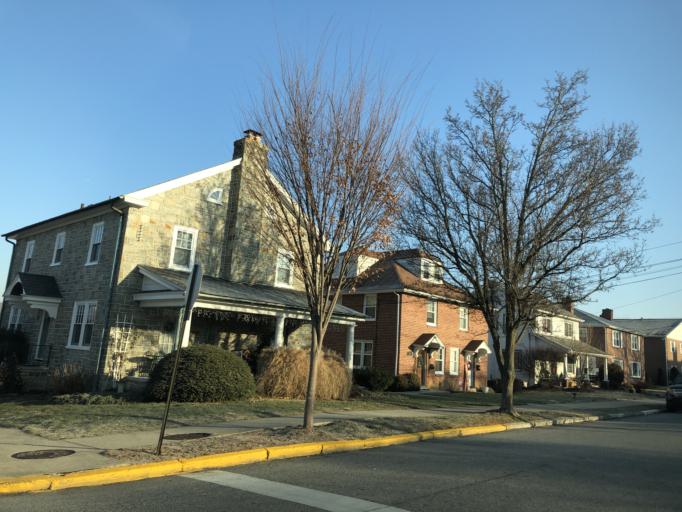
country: US
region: Pennsylvania
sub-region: Chester County
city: Downingtown
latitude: 40.0029
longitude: -75.7149
